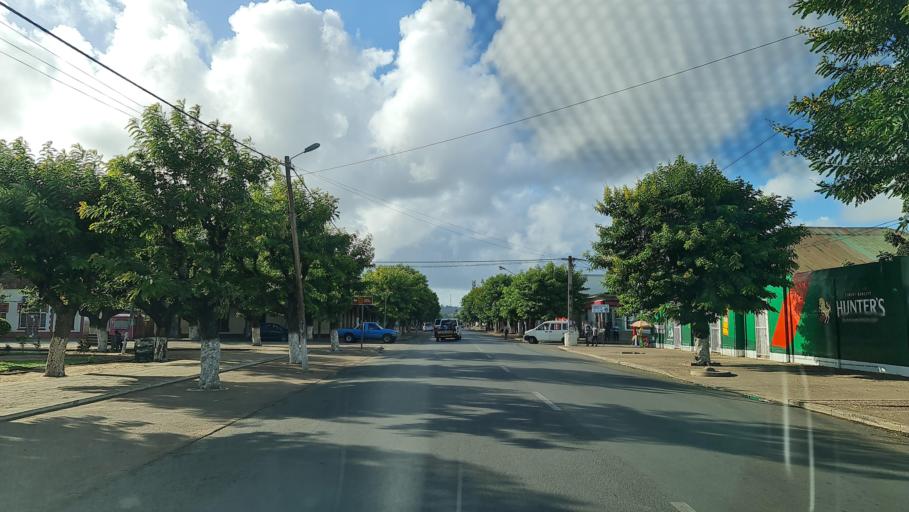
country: MZ
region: Gaza
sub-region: Xai-Xai District
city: Xai-Xai
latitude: -25.0418
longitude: 33.6411
